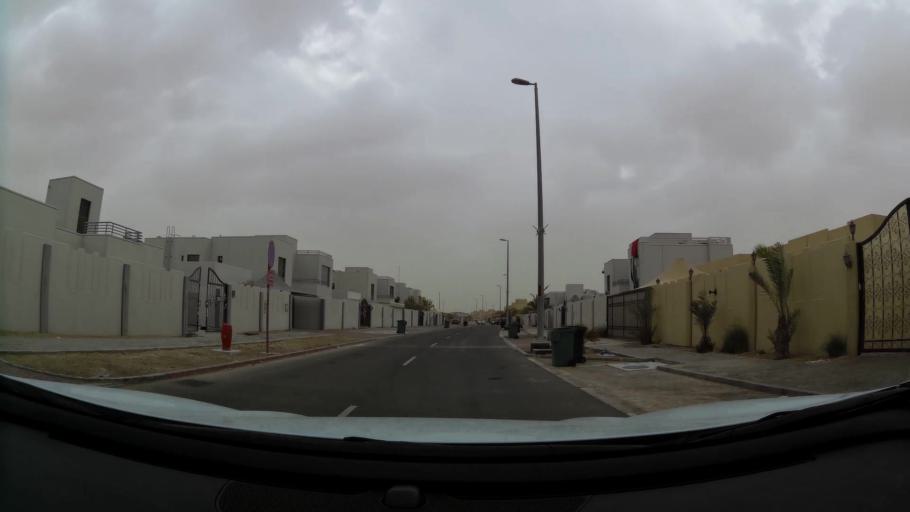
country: AE
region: Abu Dhabi
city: Abu Dhabi
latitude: 24.4557
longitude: 54.7103
